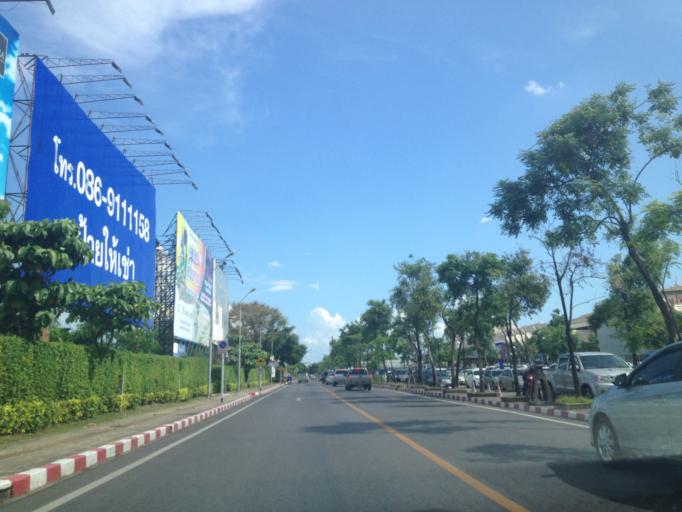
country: TH
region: Chiang Mai
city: Chiang Mai
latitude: 18.7708
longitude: 98.9690
